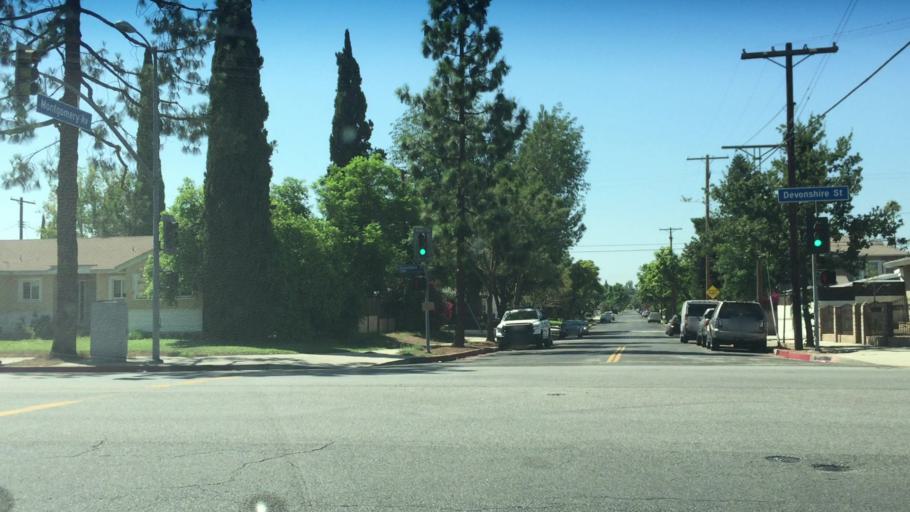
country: US
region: California
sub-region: Los Angeles County
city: San Fernando
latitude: 34.2575
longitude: -118.4817
